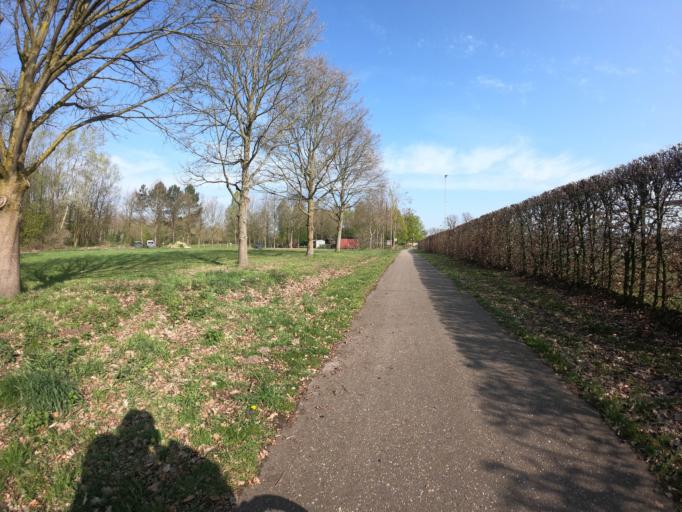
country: BE
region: Flanders
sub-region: Provincie Limburg
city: Kinrooi
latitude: 51.0837
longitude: 5.7008
